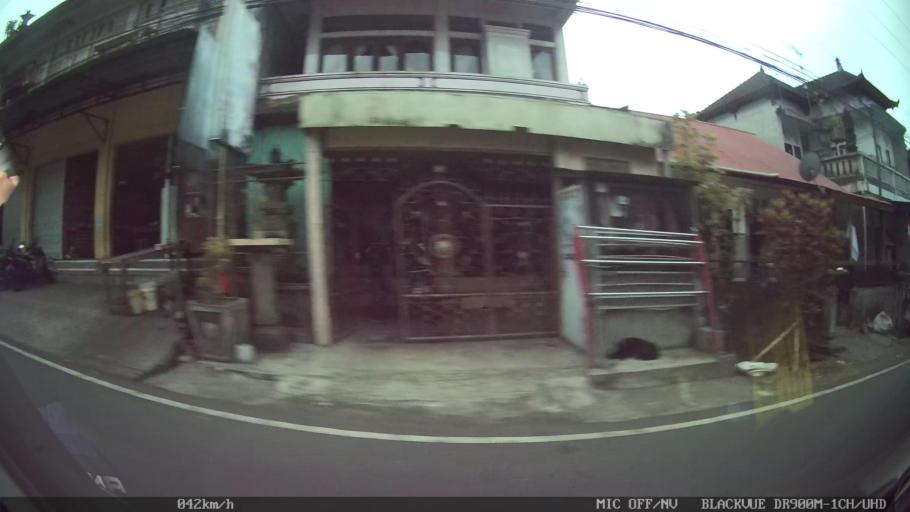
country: ID
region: Bali
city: Klau
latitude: -8.3268
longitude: 115.0296
